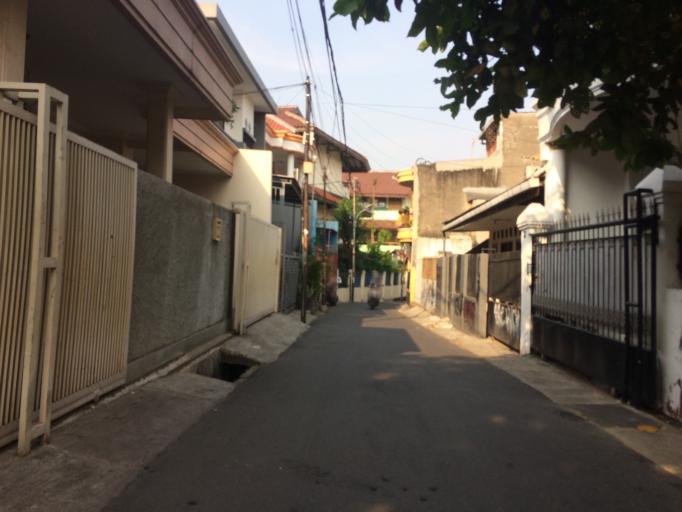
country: ID
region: Jakarta Raya
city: Jakarta
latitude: -6.2108
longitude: 106.8424
